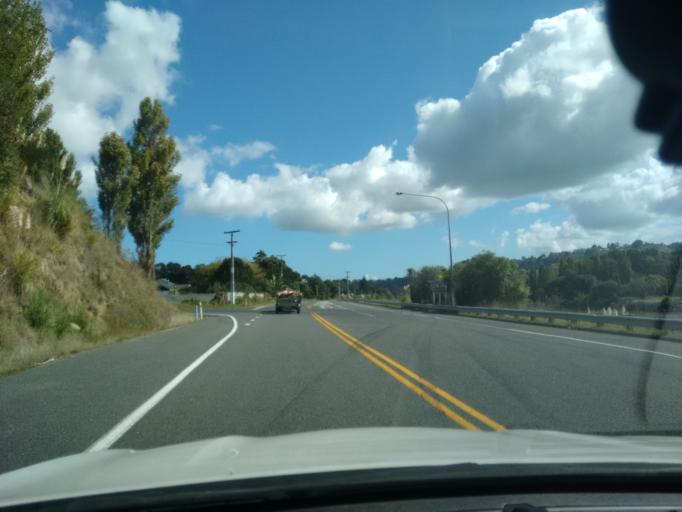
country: NZ
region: Manawatu-Wanganui
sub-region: Wanganui District
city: Wanganui
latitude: -39.8974
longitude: 175.0907
